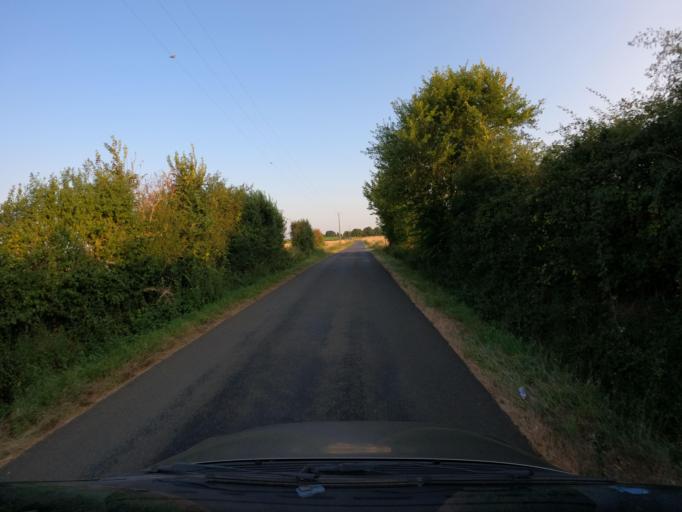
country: FR
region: Pays de la Loire
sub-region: Departement de la Sarthe
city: Parce-sur-Sarthe
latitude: 47.8951
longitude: -0.2185
